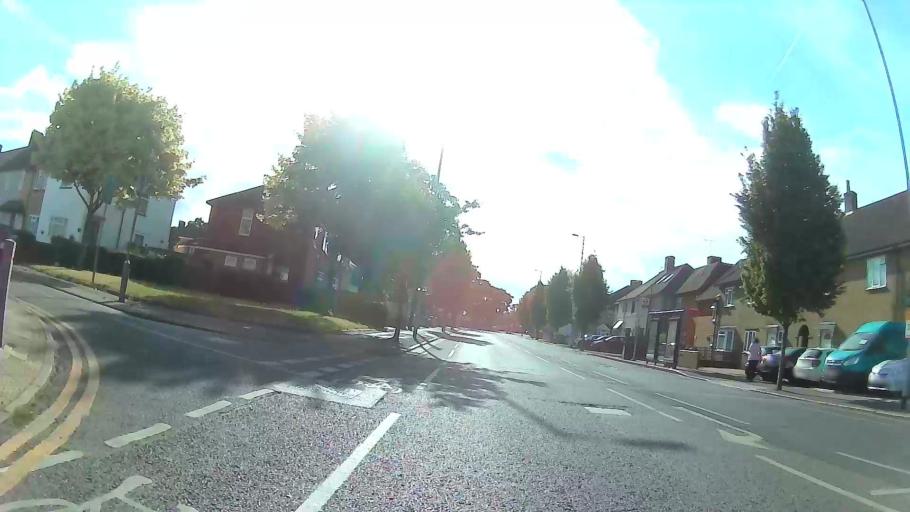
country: GB
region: England
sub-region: Greater London
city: Becontree
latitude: 51.5618
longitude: 0.1256
